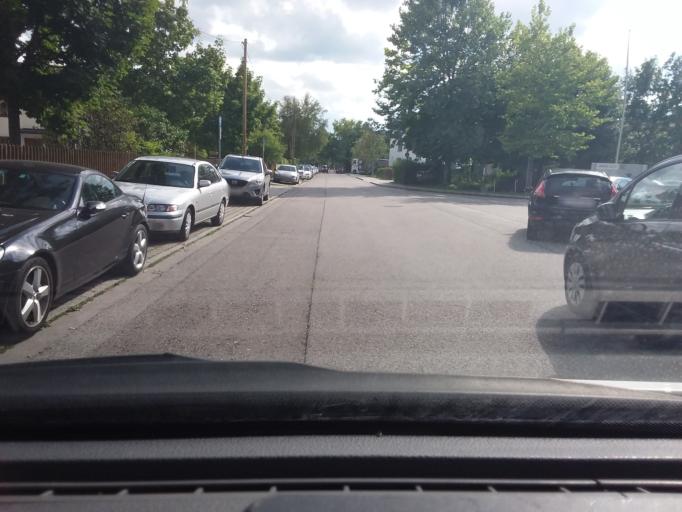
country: DE
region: Bavaria
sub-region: Upper Bavaria
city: Ismaning
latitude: 48.2318
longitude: 11.6844
